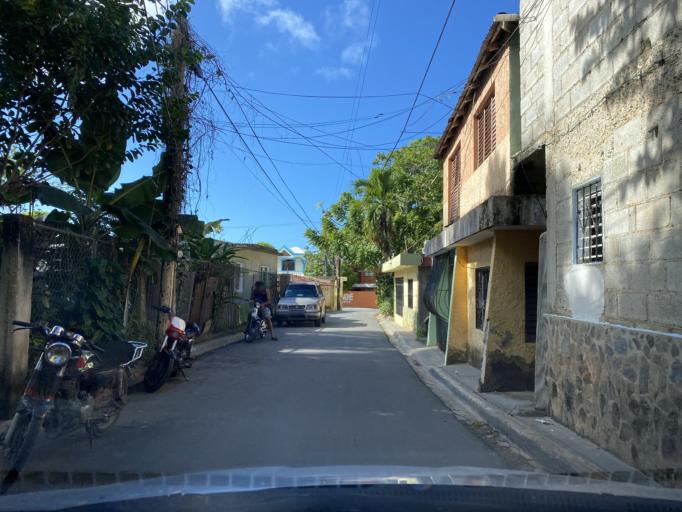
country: DO
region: Samana
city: Las Terrenas
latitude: 19.3075
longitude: -69.5453
